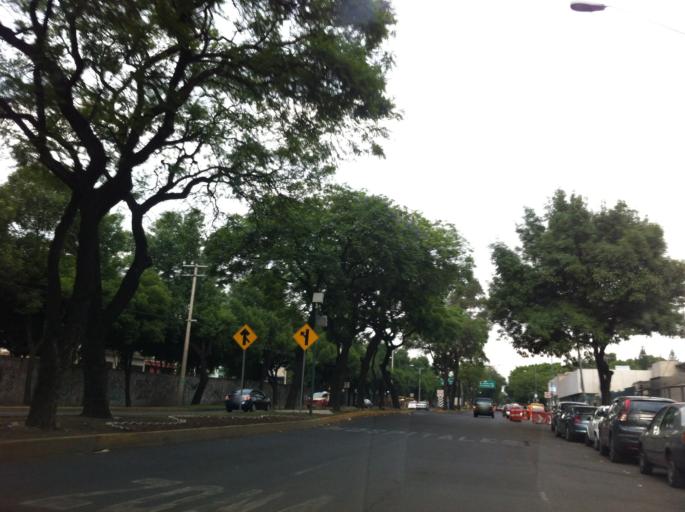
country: MX
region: Mexico
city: Colonia Lindavista
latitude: 19.4831
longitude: -99.1382
